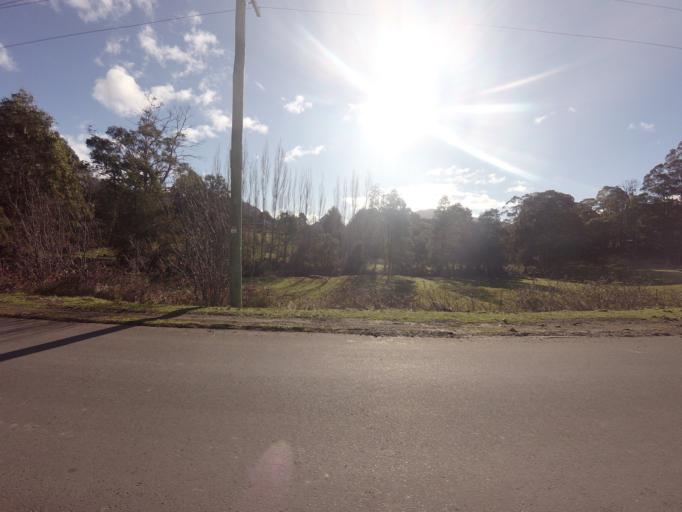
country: AU
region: Tasmania
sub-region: Glenorchy
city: Berriedale
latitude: -42.8436
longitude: 147.1904
